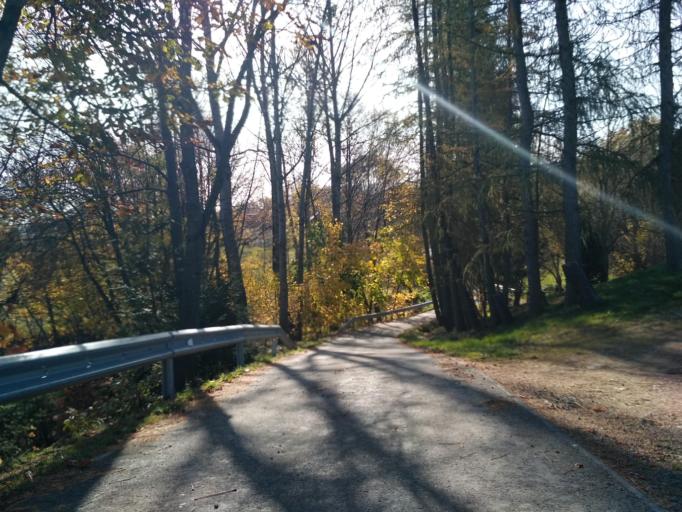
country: PL
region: Subcarpathian Voivodeship
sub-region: Powiat rzeszowski
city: Blazowa
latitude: 49.8589
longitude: 22.1286
